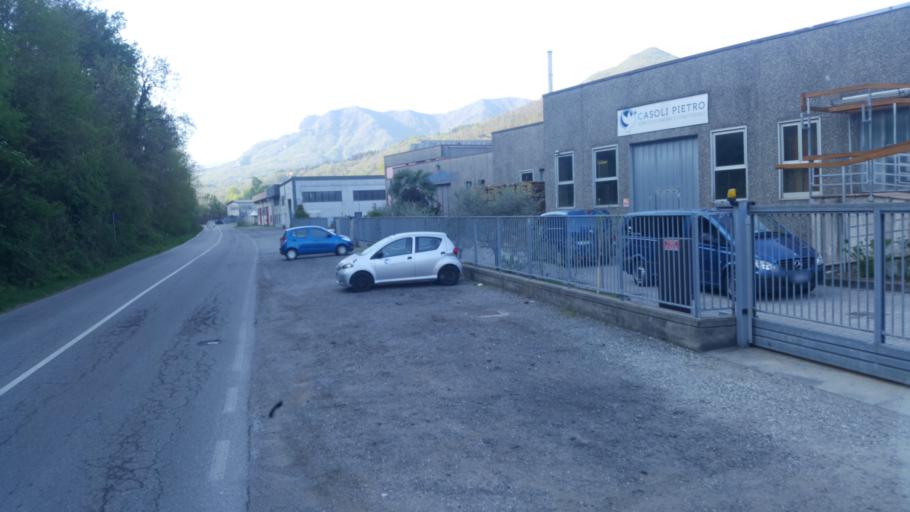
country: IT
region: Lombardy
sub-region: Provincia di Varese
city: Montegrino Valtravaglia
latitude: 45.9824
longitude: 8.7494
